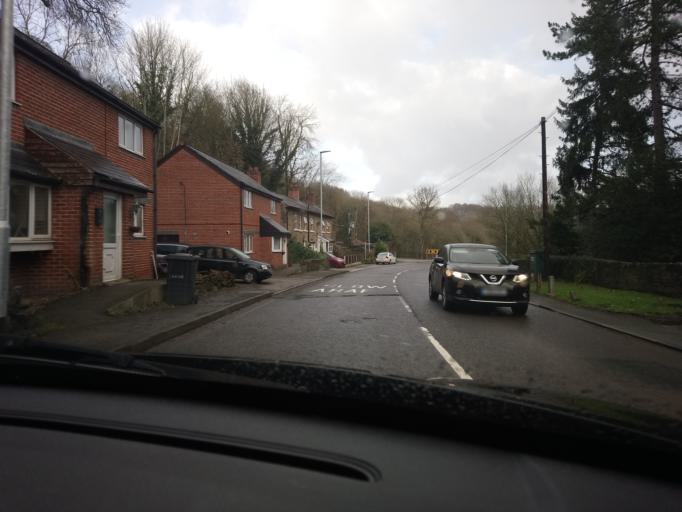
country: GB
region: Wales
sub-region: Wrexham
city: Ruabon
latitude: 52.9682
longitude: -3.0634
